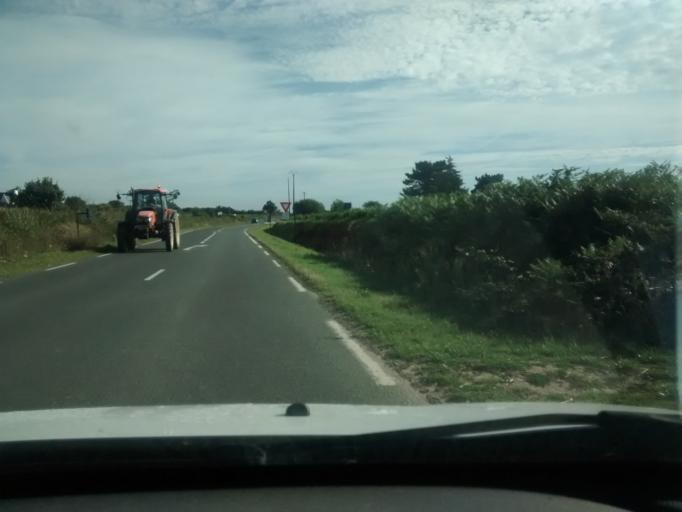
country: FR
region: Brittany
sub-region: Departement des Cotes-d'Armor
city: Penvenan
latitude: 48.7955
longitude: -3.3141
